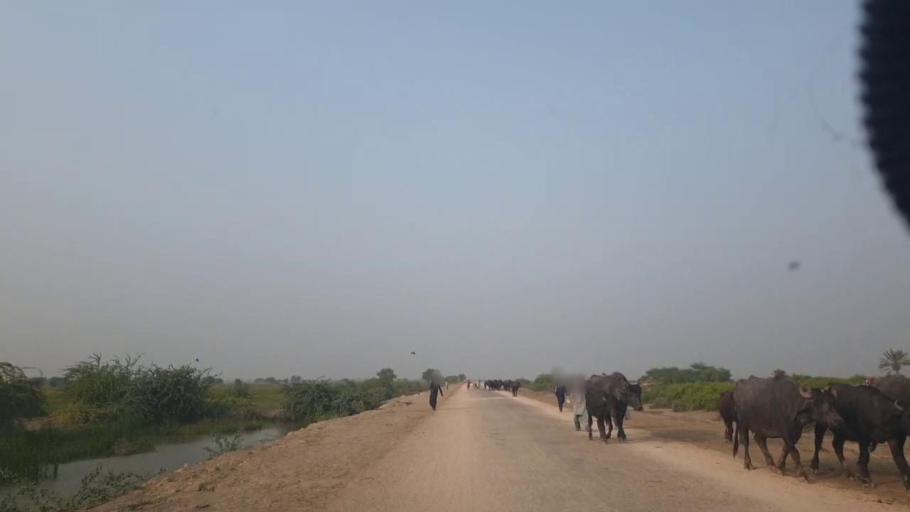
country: PK
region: Sindh
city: Bulri
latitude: 24.8403
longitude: 68.4036
